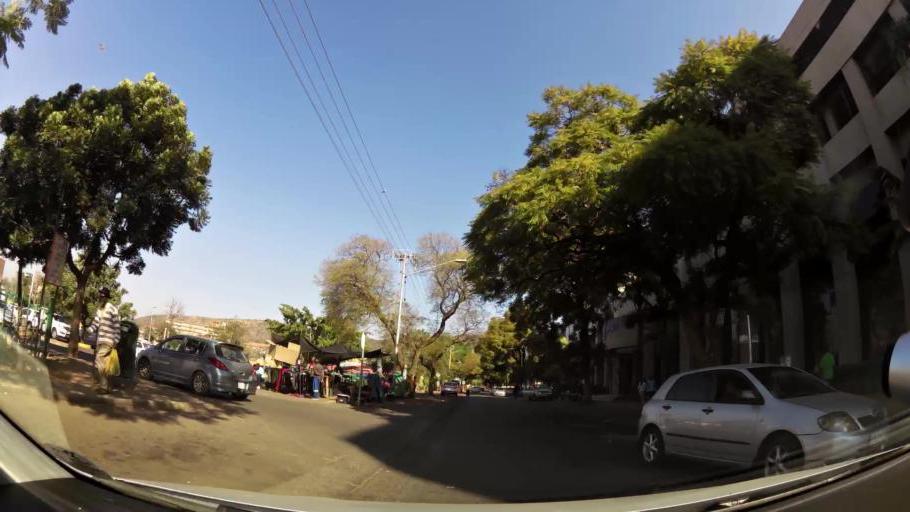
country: ZA
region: Gauteng
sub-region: City of Tshwane Metropolitan Municipality
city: Pretoria
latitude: -25.6761
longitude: 28.1725
